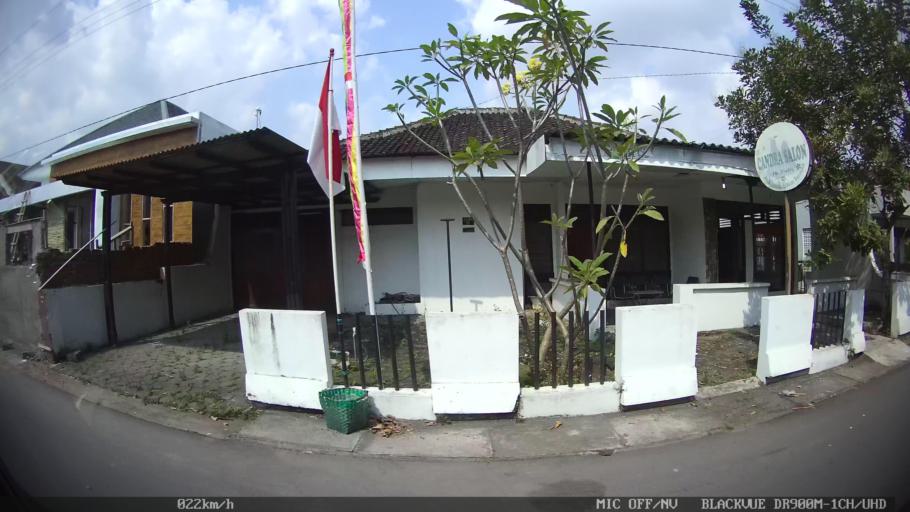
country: ID
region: Daerah Istimewa Yogyakarta
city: Yogyakarta
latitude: -7.8211
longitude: 110.3962
